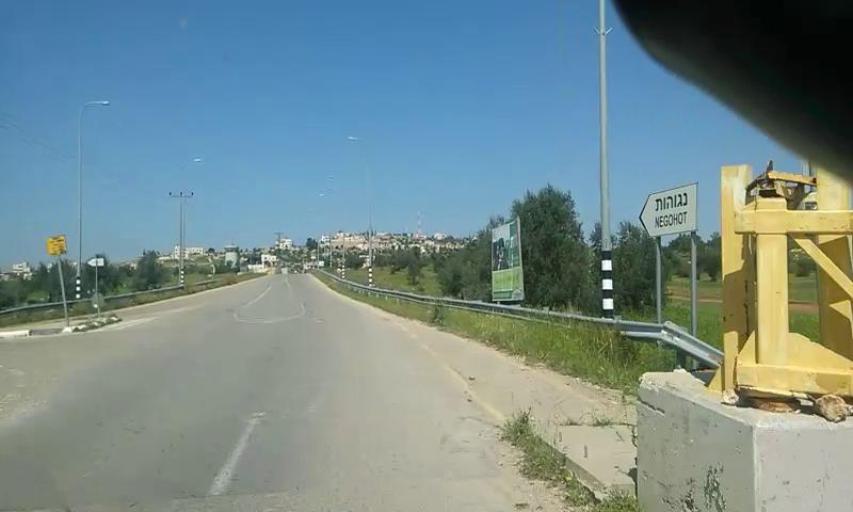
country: PS
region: West Bank
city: Bayt `Awwa
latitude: 31.4980
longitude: 34.9616
